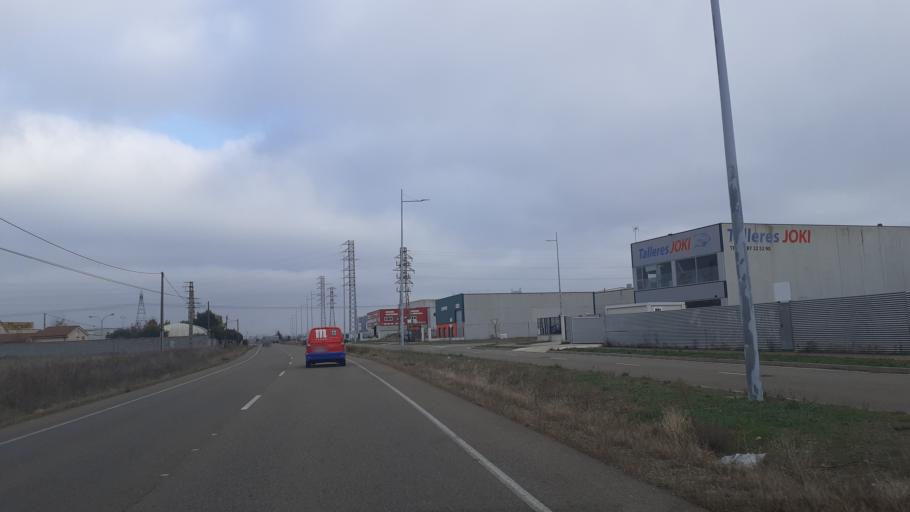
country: ES
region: Castille and Leon
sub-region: Provincia de Leon
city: Onzonilla
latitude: 42.5502
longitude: -5.5856
